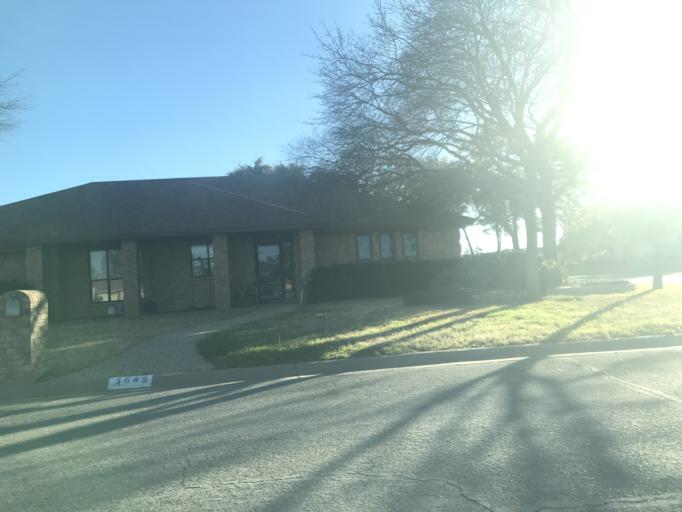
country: US
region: Texas
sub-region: Tom Green County
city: San Angelo
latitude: 31.4265
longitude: -100.4950
